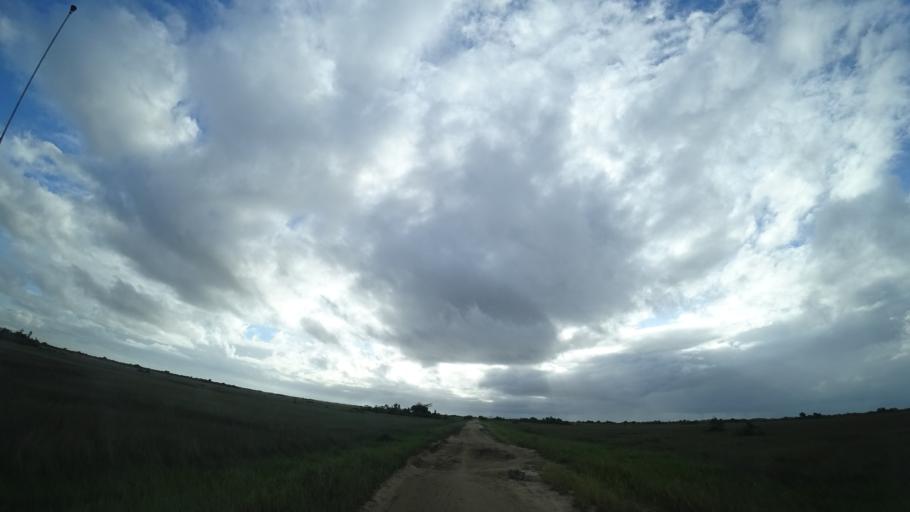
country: MZ
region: Sofala
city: Beira
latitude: -19.7036
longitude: 35.0222
